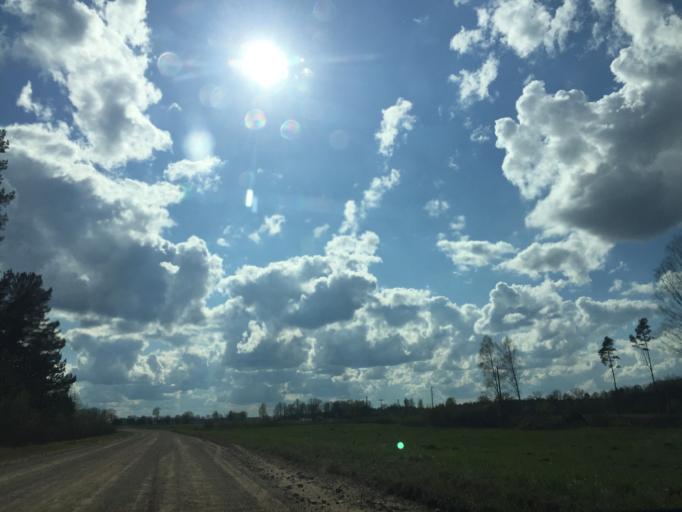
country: LV
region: Beverina
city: Murmuiza
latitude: 57.4117
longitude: 25.5349
